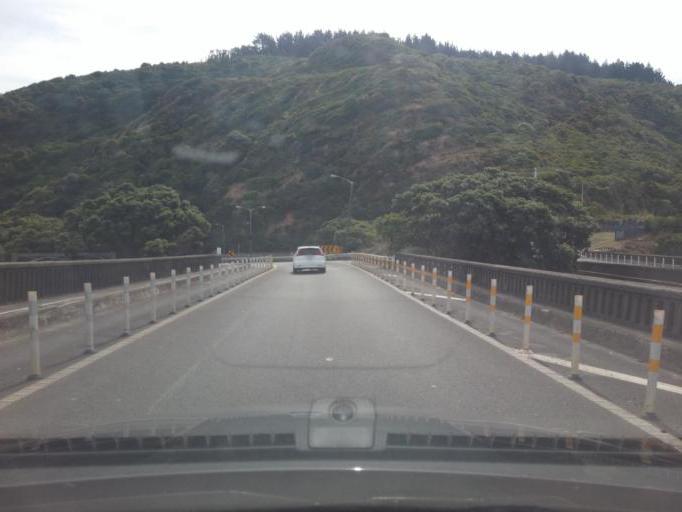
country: NZ
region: Wellington
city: Petone
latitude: -41.2243
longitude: 174.8603
